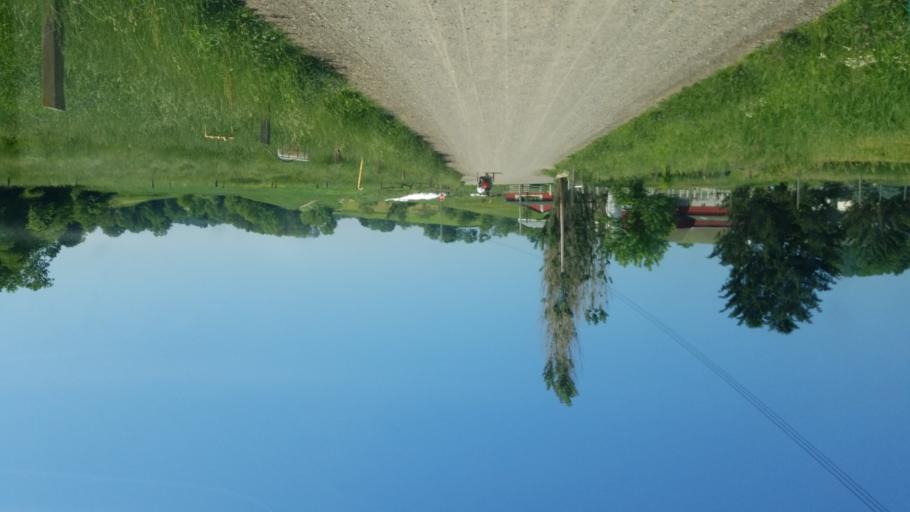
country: US
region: Ohio
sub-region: Holmes County
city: Millersburg
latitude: 40.4631
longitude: -81.7970
